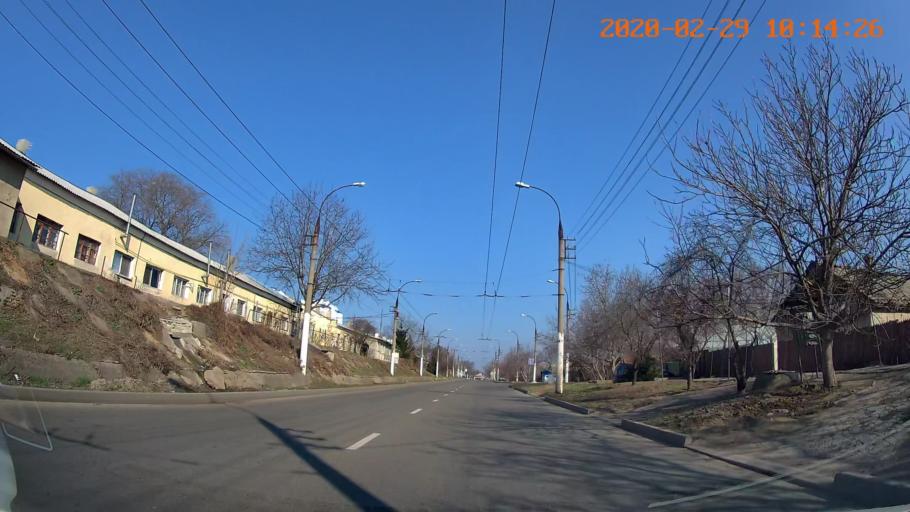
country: MD
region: Telenesti
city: Tiraspolul Nou
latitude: 46.8467
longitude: 29.6435
